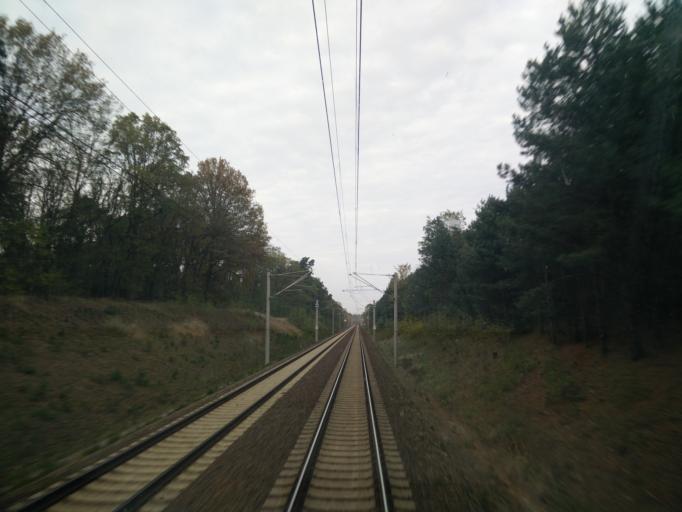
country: DE
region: Brandenburg
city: Halbe
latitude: 52.0441
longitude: 13.7197
